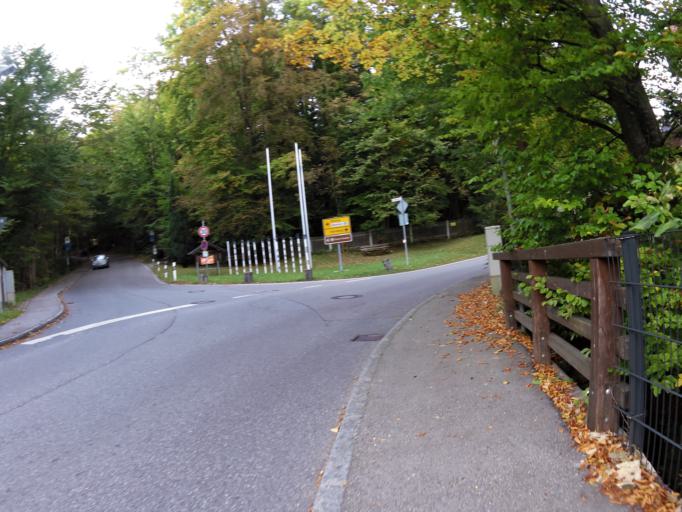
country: DE
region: Bavaria
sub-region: Upper Bavaria
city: Pocking
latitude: 47.9599
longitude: 11.3094
